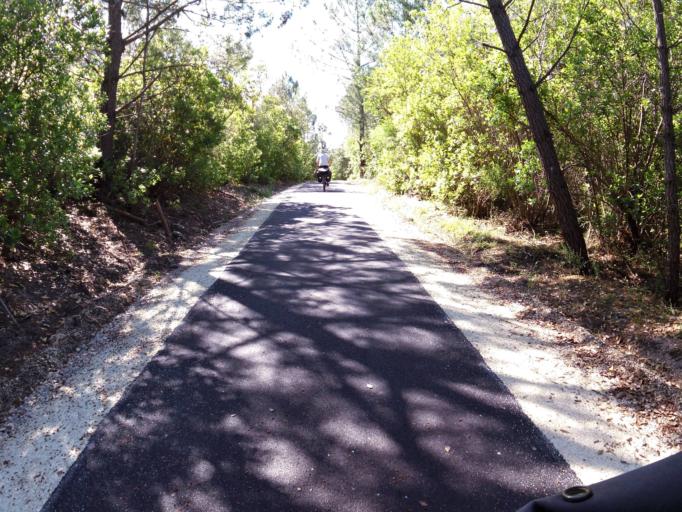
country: FR
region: Aquitaine
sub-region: Departement de la Gironde
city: Lacanau
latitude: 45.0317
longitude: -1.1766
